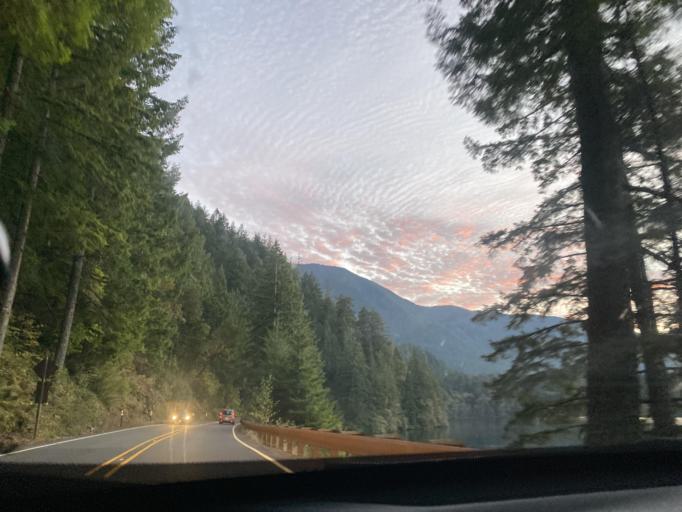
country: CA
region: British Columbia
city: Sooke
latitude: 48.0618
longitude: -123.7783
